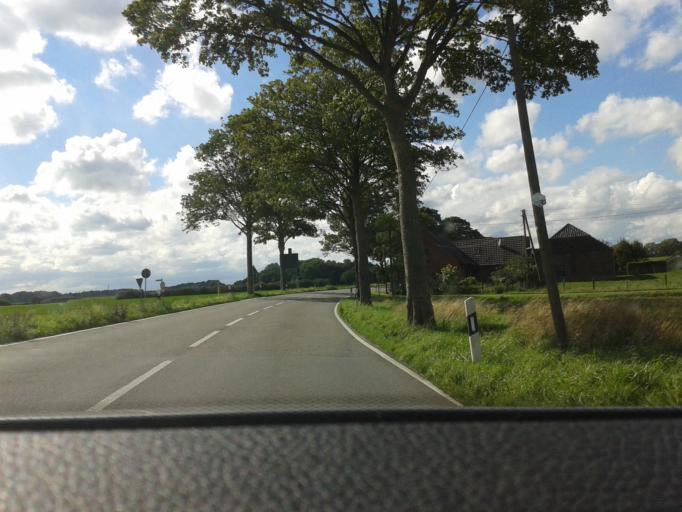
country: DE
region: North Rhine-Westphalia
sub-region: Regierungsbezirk Dusseldorf
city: Uedem
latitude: 51.6252
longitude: 6.2767
